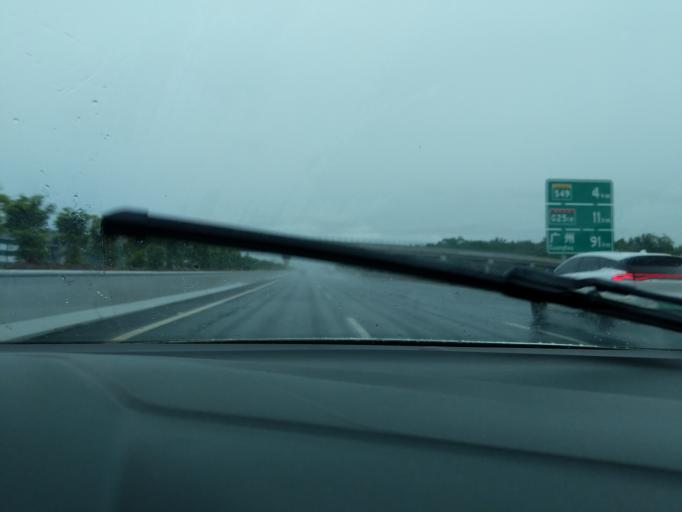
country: CN
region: Guangdong
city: Zhishan
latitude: 22.4850
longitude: 112.7862
